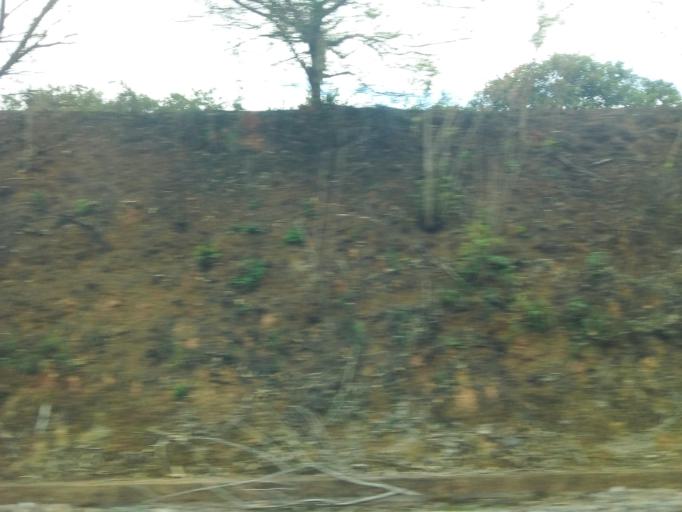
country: BR
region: Minas Gerais
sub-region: Governador Valadares
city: Governador Valadares
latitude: -19.0678
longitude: -42.1505
